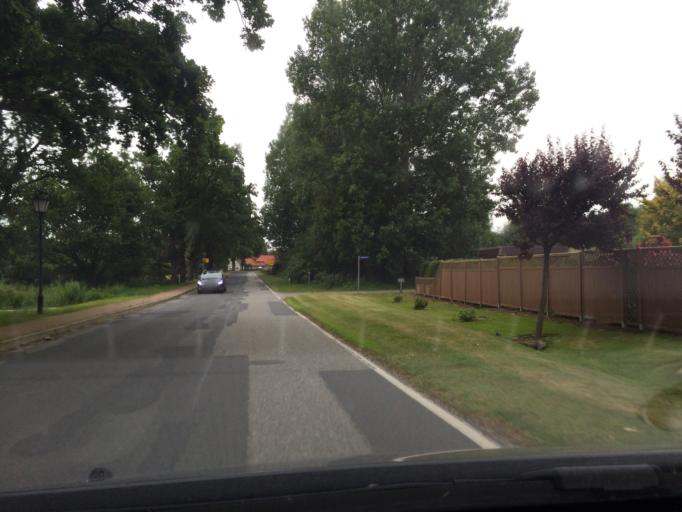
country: DE
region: Mecklenburg-Vorpommern
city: Prohn
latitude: 54.4097
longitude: 13.0149
